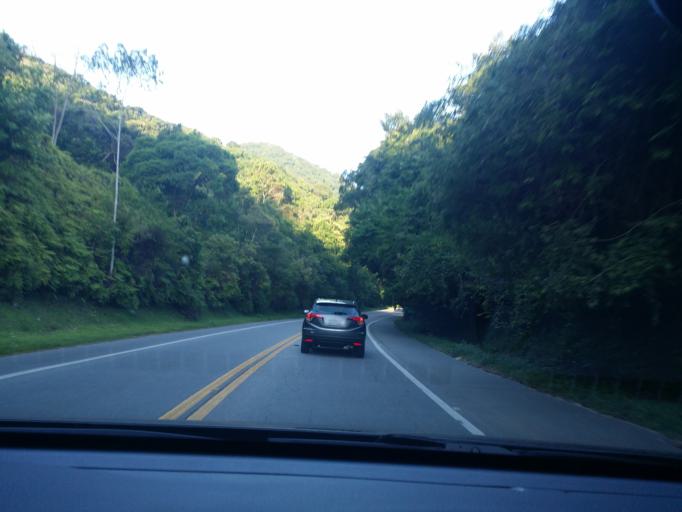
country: BR
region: Sao Paulo
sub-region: Sao Sebastiao
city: Sao Sebastiao
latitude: -23.7714
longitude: -45.7167
